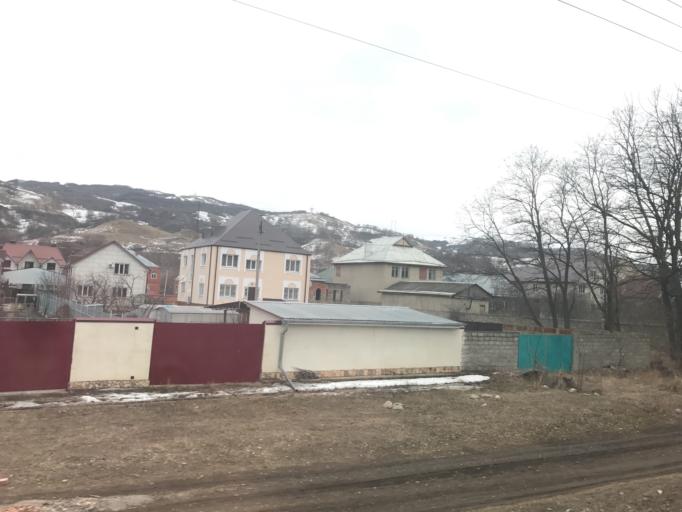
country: RU
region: Stavropol'skiy
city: Kislovodsk
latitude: 43.9564
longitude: 42.7617
